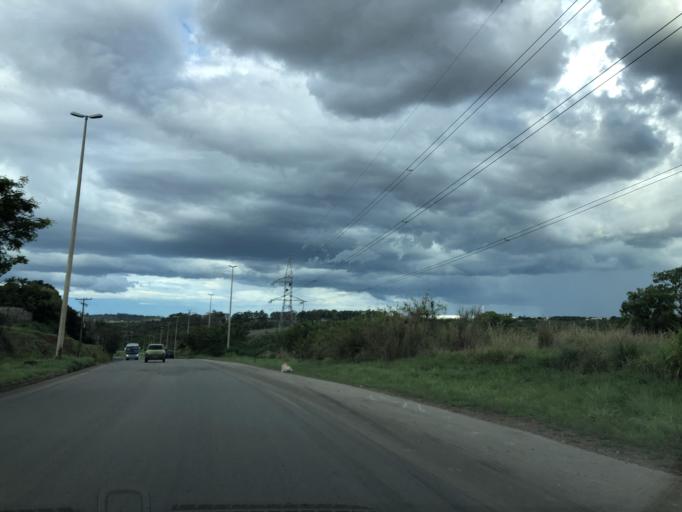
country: BR
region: Goias
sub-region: Luziania
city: Luziania
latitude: -16.0420
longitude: -48.0577
